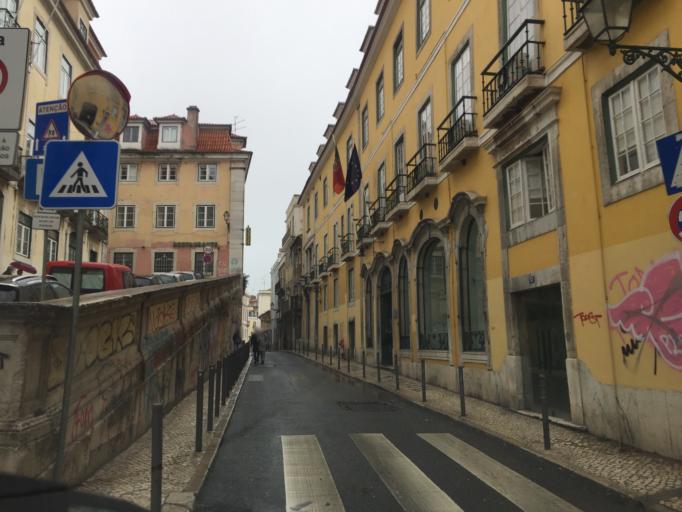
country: PT
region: Lisbon
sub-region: Lisbon
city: Lisbon
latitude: 38.7125
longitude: -9.1476
